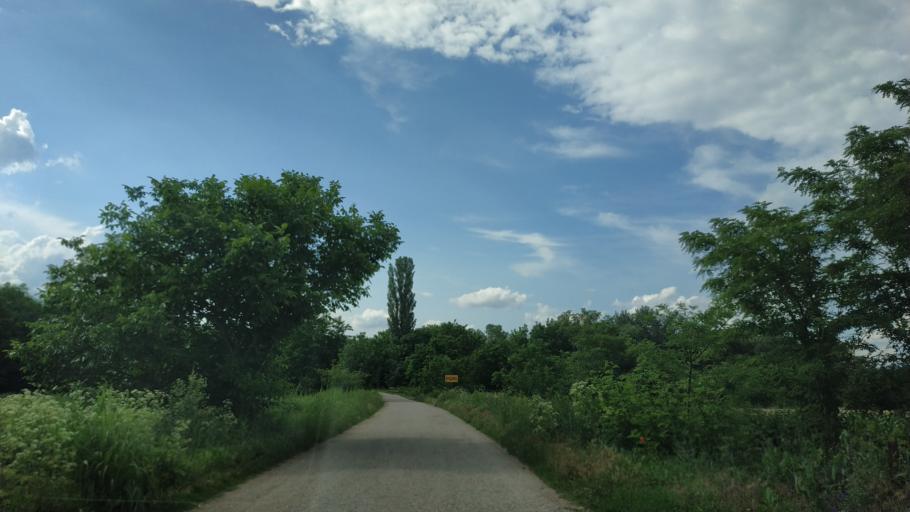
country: RS
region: Central Serbia
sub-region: Nisavski Okrug
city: Aleksinac
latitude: 43.6127
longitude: 21.6484
